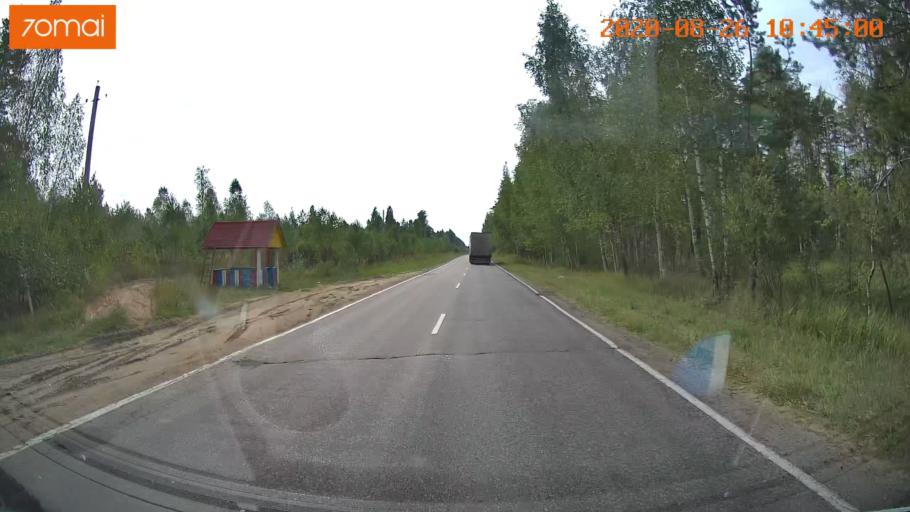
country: RU
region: Rjazan
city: Lashma
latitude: 54.7628
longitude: 41.1848
